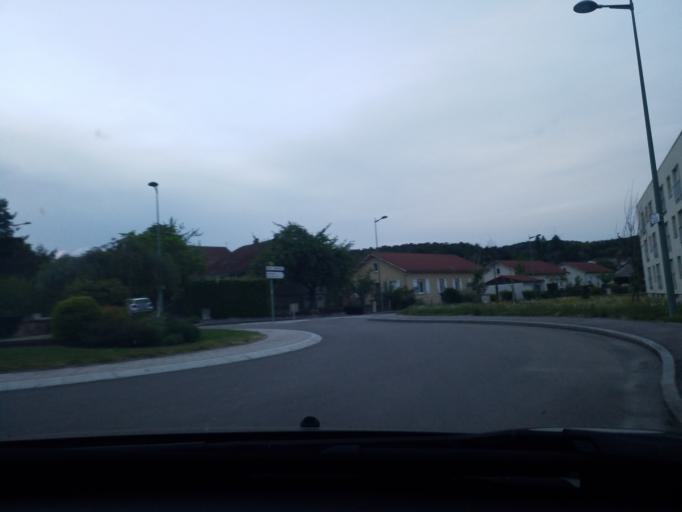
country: FR
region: Lorraine
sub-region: Departement des Vosges
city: Vittel
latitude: 48.2065
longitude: 5.9534
